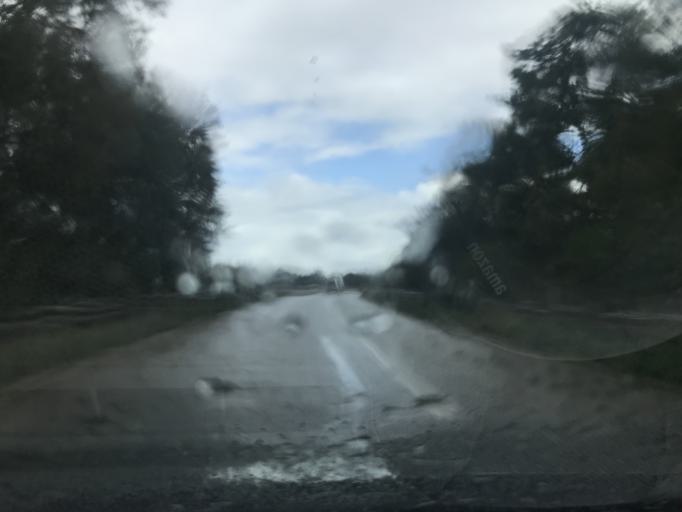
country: DE
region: North Rhine-Westphalia
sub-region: Regierungsbezirk Dusseldorf
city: Kaarst
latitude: 51.2344
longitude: 6.6393
